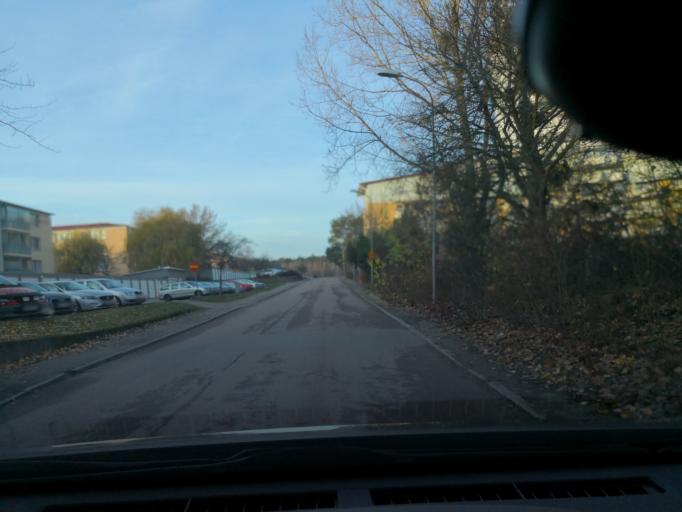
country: SE
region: Vaestmanland
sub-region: Vasteras
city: Vasteras
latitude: 59.6094
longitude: 16.4907
